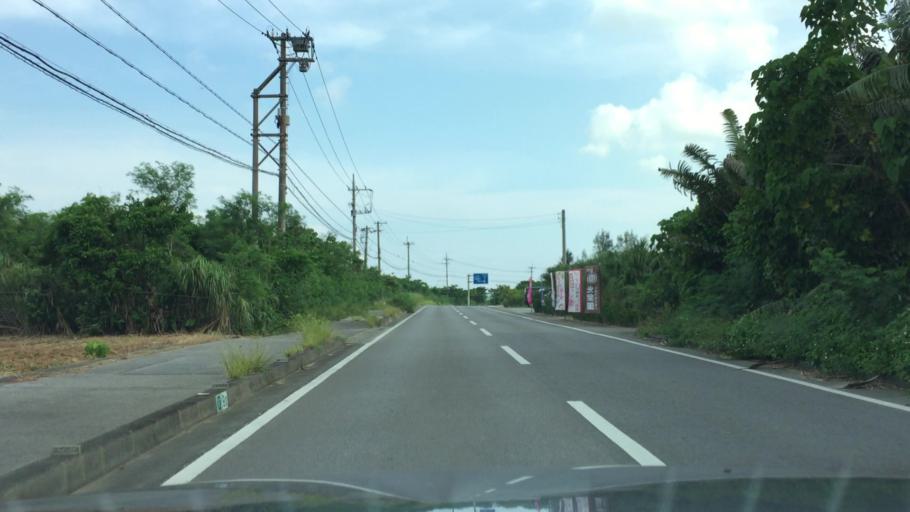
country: JP
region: Okinawa
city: Ishigaki
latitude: 24.3961
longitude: 124.1953
